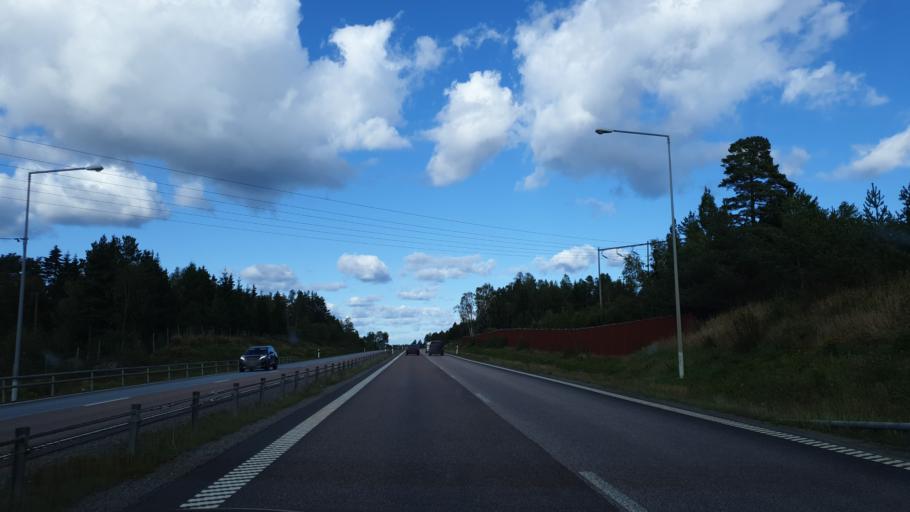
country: SE
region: Gaevleborg
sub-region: Soderhamns Kommun
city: Soderhamn
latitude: 61.3053
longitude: 17.0324
